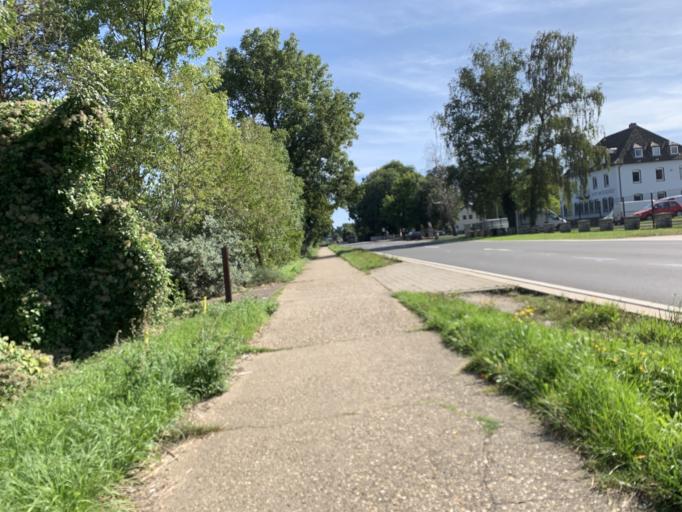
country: DE
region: North Rhine-Westphalia
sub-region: Regierungsbezirk Koln
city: Dueren
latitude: 50.8050
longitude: 6.4610
